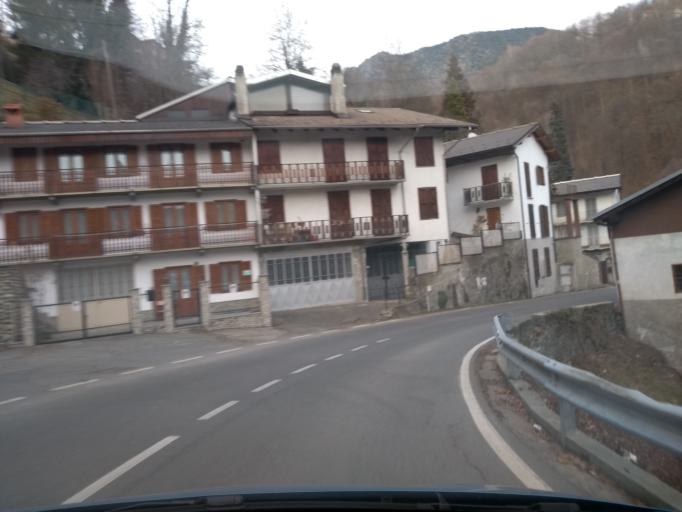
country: IT
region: Piedmont
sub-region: Provincia di Torino
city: Viu
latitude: 45.2403
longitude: 7.3785
